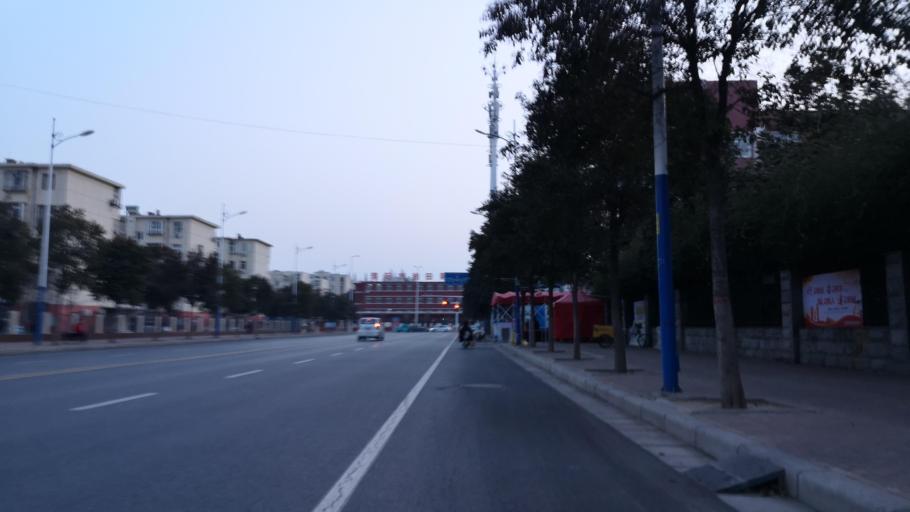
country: CN
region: Henan Sheng
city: Zhongyuanlu
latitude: 35.7646
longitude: 115.0626
